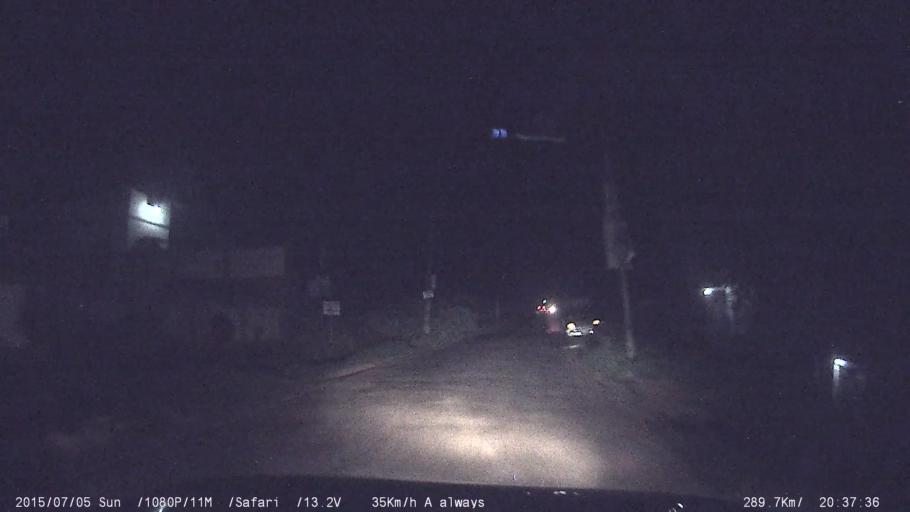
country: IN
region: Kerala
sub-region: Palakkad district
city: Mannarakkat
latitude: 10.9815
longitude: 76.4933
